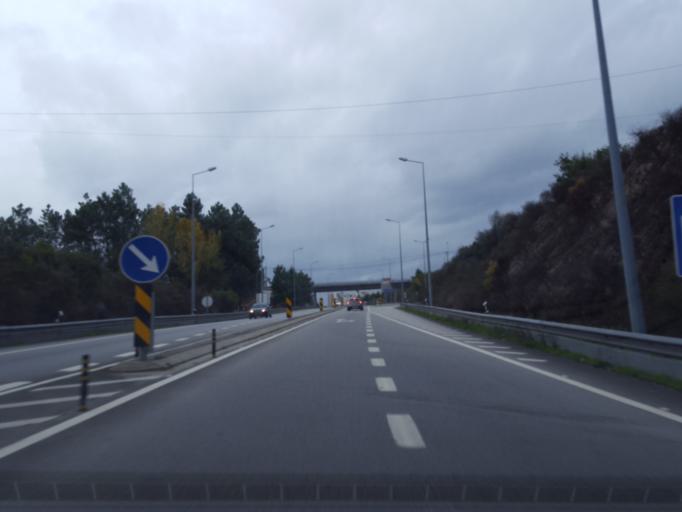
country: PT
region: Porto
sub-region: Marco de Canaveses
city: Marco de Canavezes
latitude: 41.2078
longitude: -8.1660
